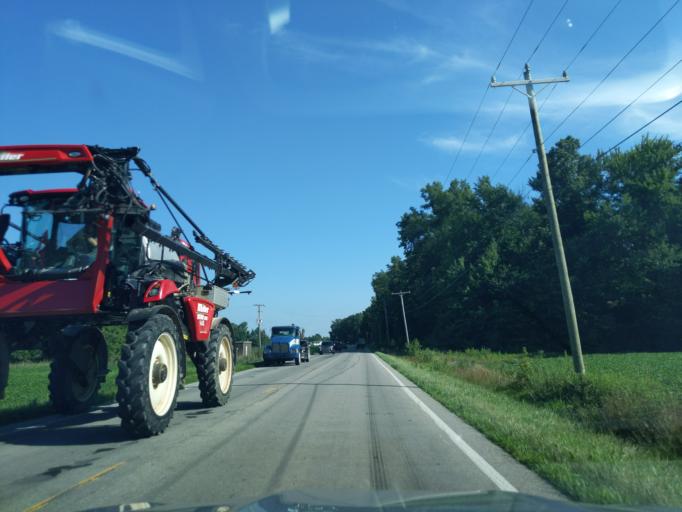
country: US
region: Indiana
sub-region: Ripley County
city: Osgood
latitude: 39.1483
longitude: -85.3003
